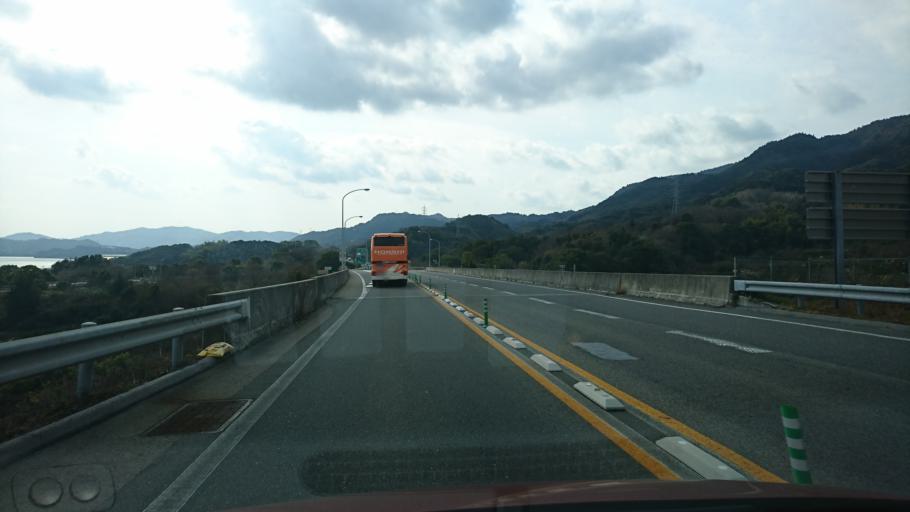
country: JP
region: Hiroshima
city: Innoshima
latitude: 34.2524
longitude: 133.0497
